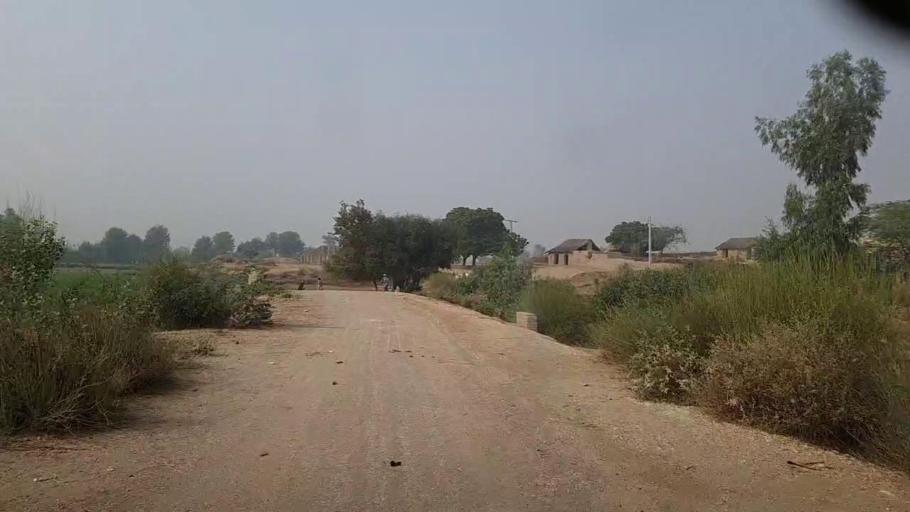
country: PK
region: Sindh
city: Kandiari
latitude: 26.9788
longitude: 68.5908
